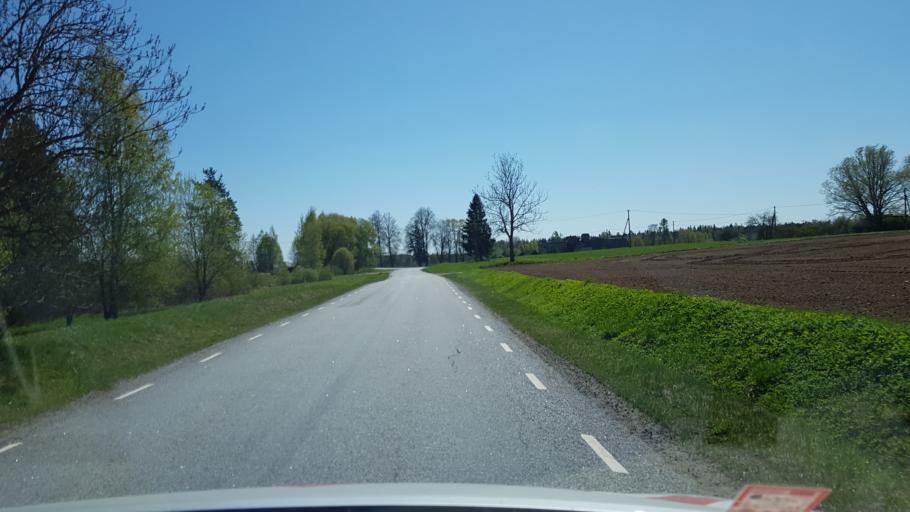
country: EE
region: Vorumaa
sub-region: Voru linn
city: Voru
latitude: 57.9134
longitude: 26.9569
